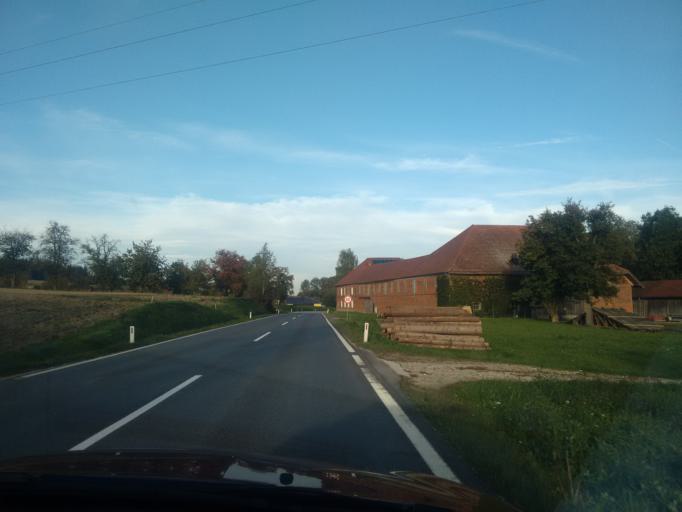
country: AT
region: Upper Austria
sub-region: Wels-Land
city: Bachmanning
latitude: 48.1699
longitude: 13.7558
